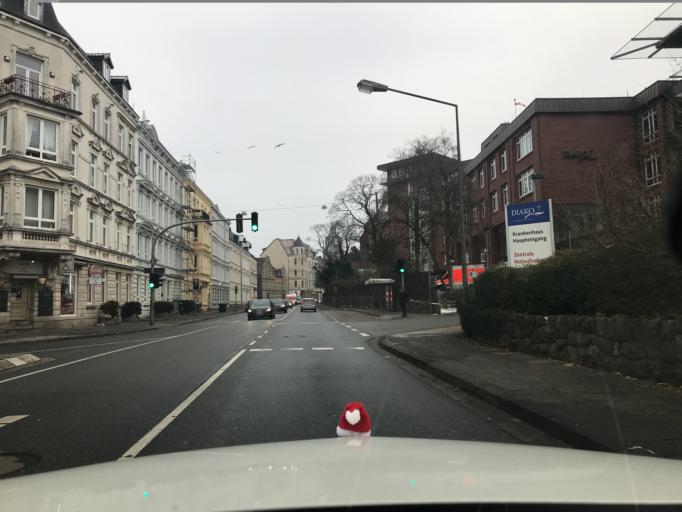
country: DE
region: Schleswig-Holstein
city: Flensburg
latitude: 54.7912
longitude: 9.4253
